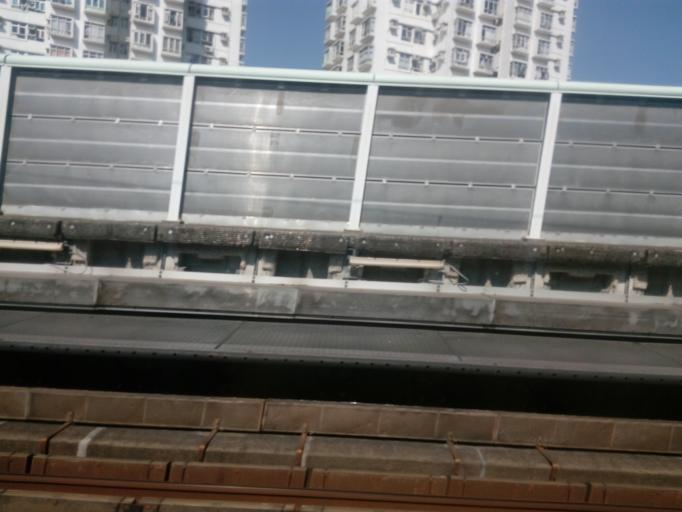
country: HK
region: Sha Tin
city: Sha Tin
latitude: 22.3804
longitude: 114.2000
